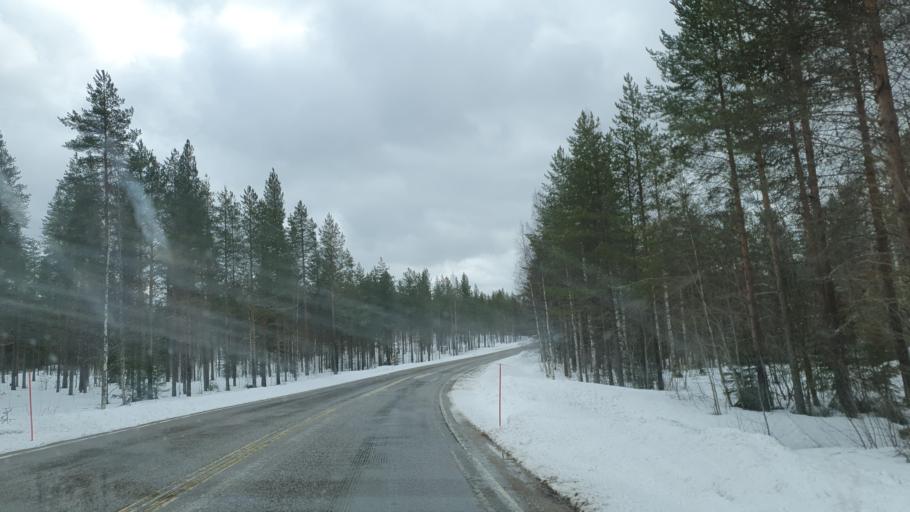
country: FI
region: Kainuu
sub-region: Kehys-Kainuu
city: Puolanka
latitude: 65.1348
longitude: 27.6906
